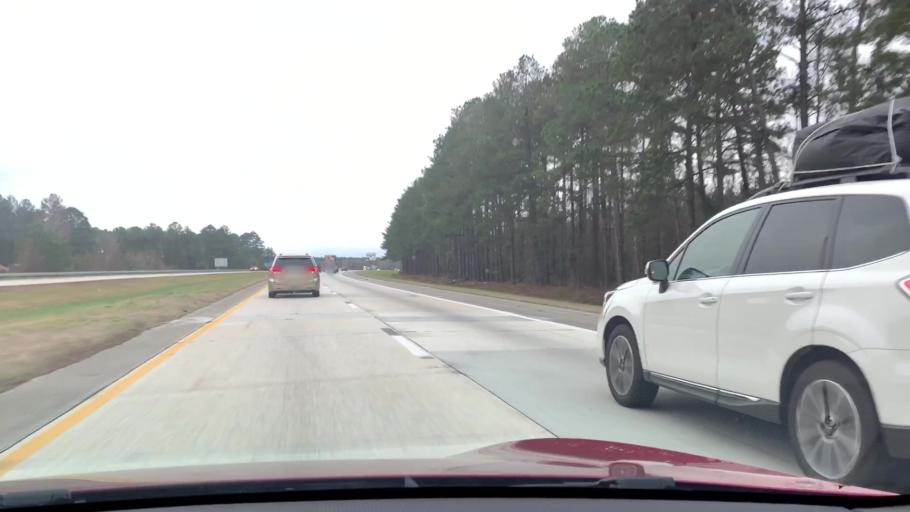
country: US
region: South Carolina
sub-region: Florence County
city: Timmonsville
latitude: 34.1450
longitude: -79.8769
